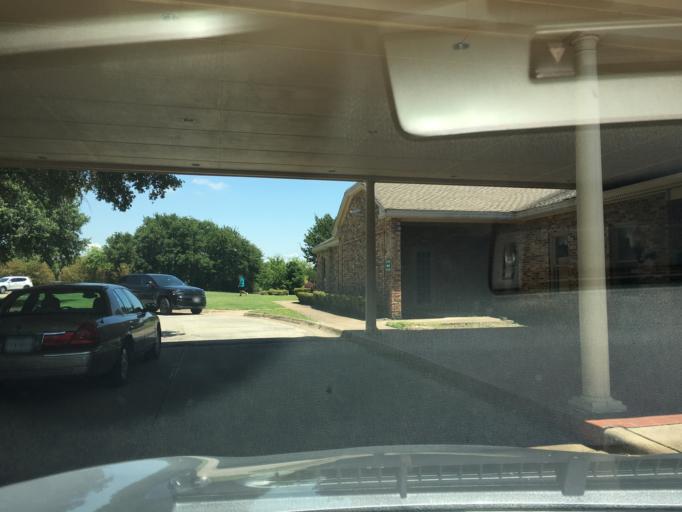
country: US
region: Texas
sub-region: Dallas County
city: Garland
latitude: 32.9404
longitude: -96.6738
